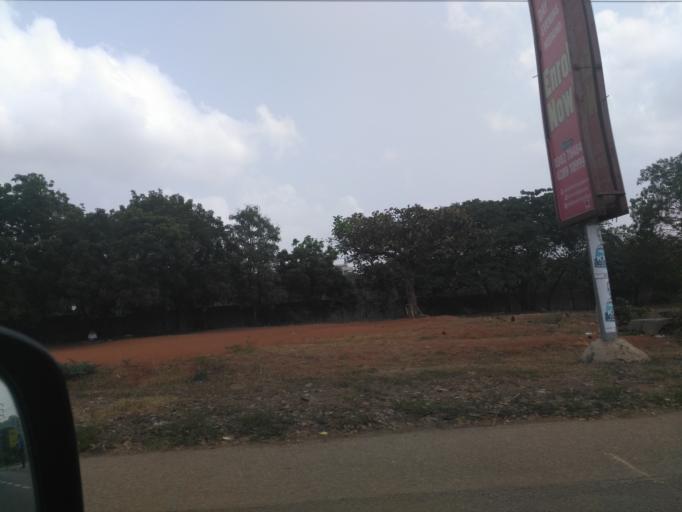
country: GH
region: Greater Accra
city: Accra
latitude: 5.5964
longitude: -0.1905
